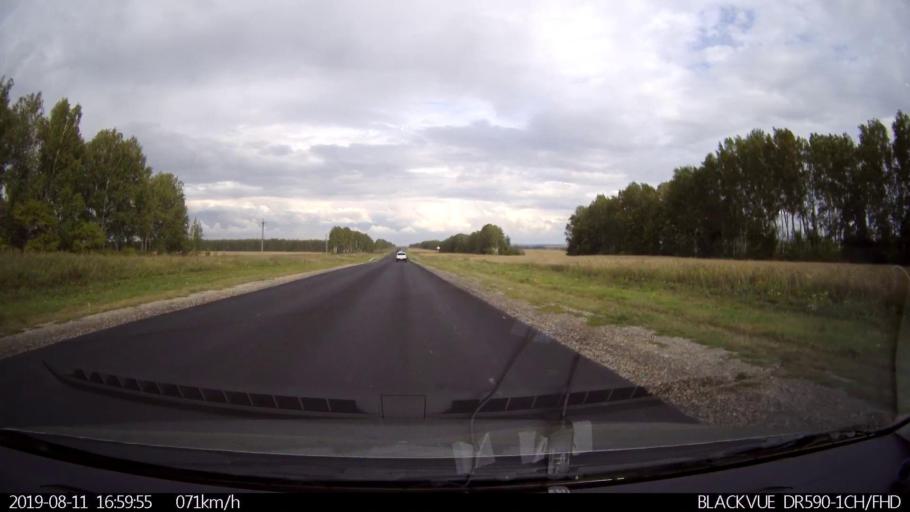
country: RU
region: Ulyanovsk
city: Mayna
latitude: 54.3115
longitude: 47.6703
